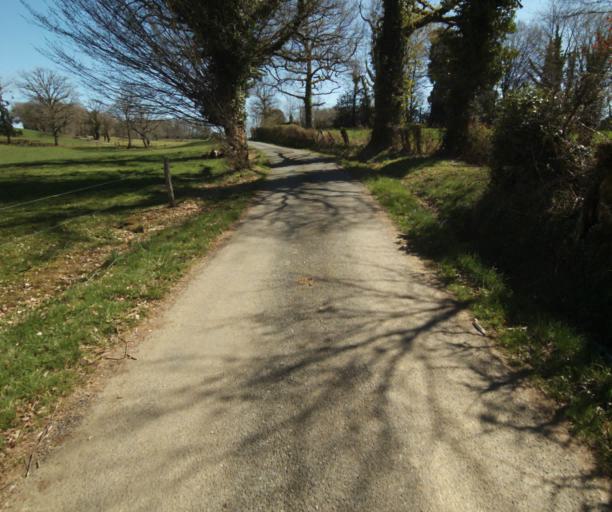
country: FR
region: Limousin
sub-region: Departement de la Correze
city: Uzerche
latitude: 45.3971
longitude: 1.6329
